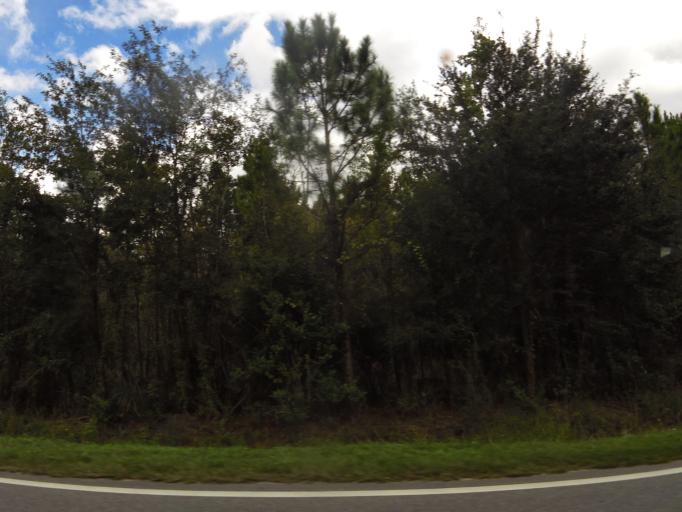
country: US
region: Florida
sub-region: Saint Johns County
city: Villano Beach
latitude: 29.9882
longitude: -81.4429
